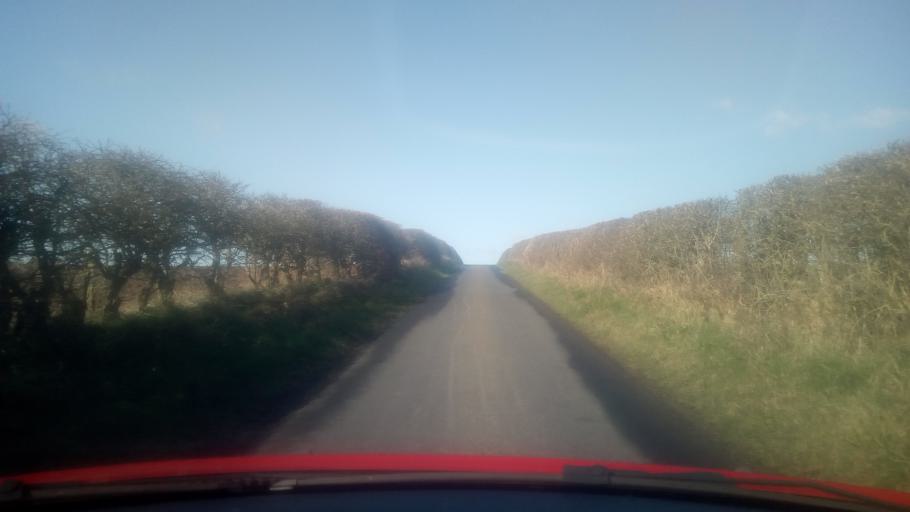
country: GB
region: Scotland
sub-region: The Scottish Borders
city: Saint Boswells
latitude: 55.5225
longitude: -2.6068
